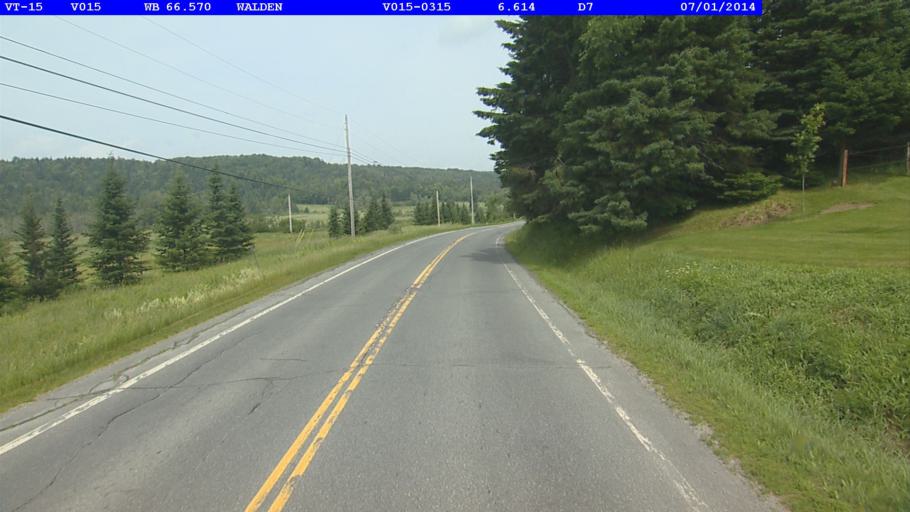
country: US
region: Vermont
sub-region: Caledonia County
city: Hardwick
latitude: 44.4305
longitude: -72.2206
